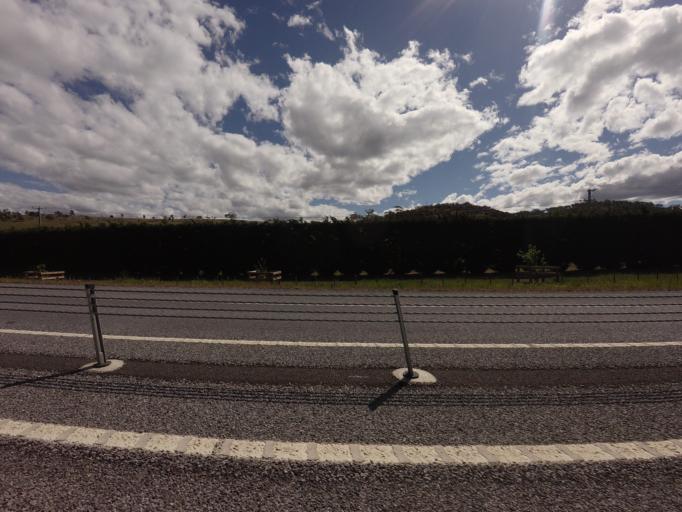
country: AU
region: Tasmania
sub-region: Northern Midlands
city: Evandale
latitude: -42.0615
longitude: 147.4835
